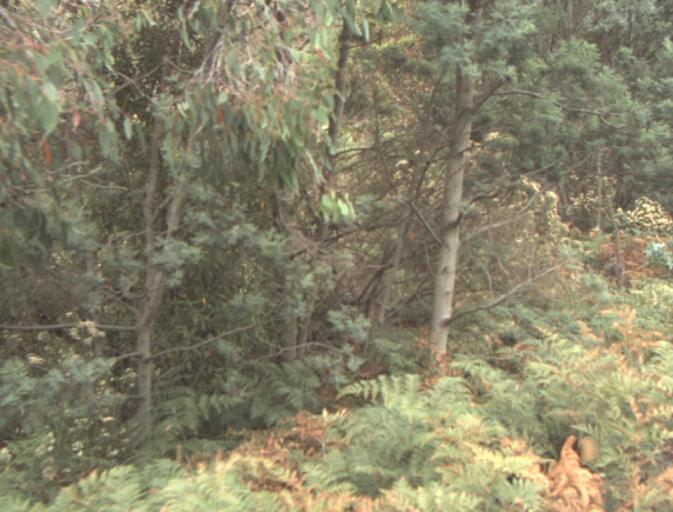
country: AU
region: Tasmania
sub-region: Northern Midlands
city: Evandale
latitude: -41.5187
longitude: 147.4140
